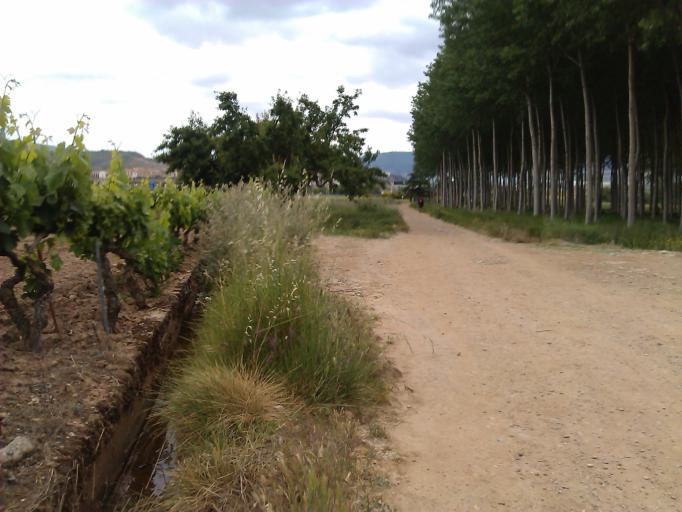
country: ES
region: La Rioja
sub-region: Provincia de La Rioja
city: Navarrete
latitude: 42.4361
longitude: -2.5451
